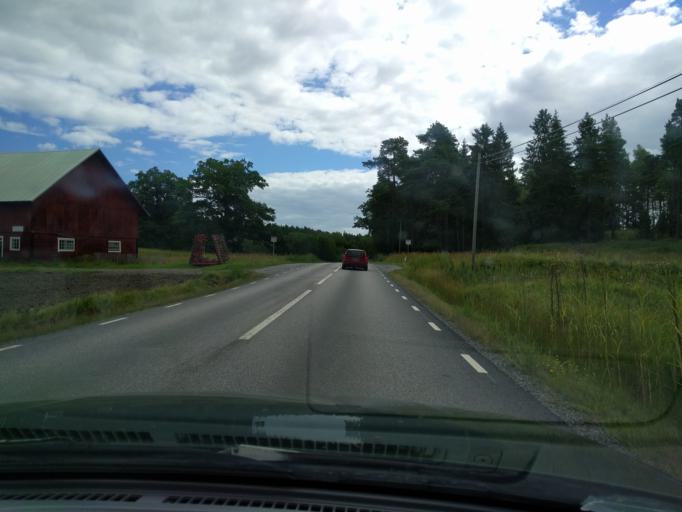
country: SE
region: Soedermanland
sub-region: Nykopings Kommun
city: Svalsta
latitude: 58.5206
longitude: 16.7781
